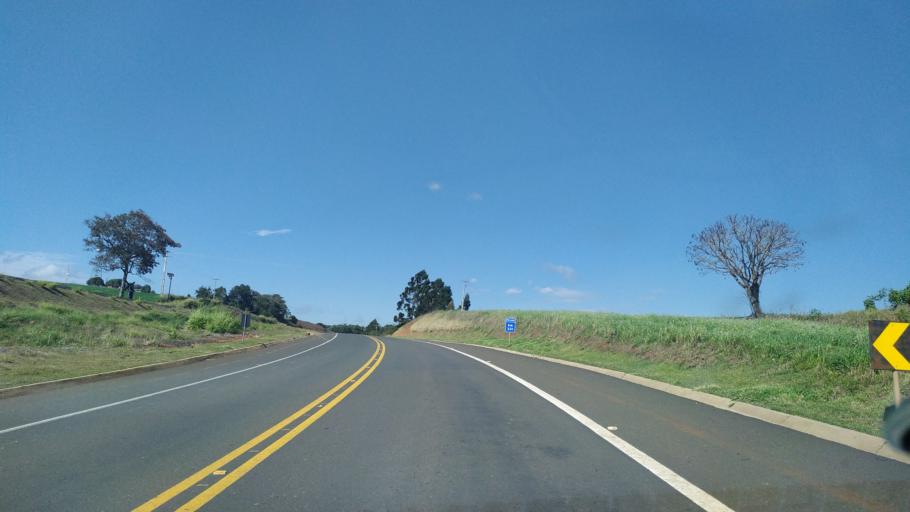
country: BR
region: Parana
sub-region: Ortigueira
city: Ortigueira
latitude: -24.2663
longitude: -50.8101
